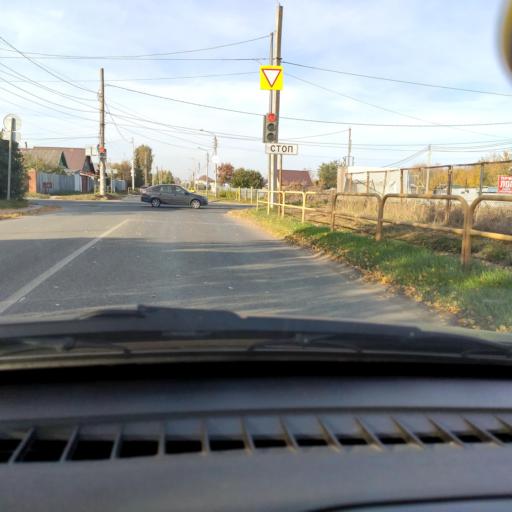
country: RU
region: Samara
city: Tol'yatti
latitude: 53.5347
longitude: 49.4289
